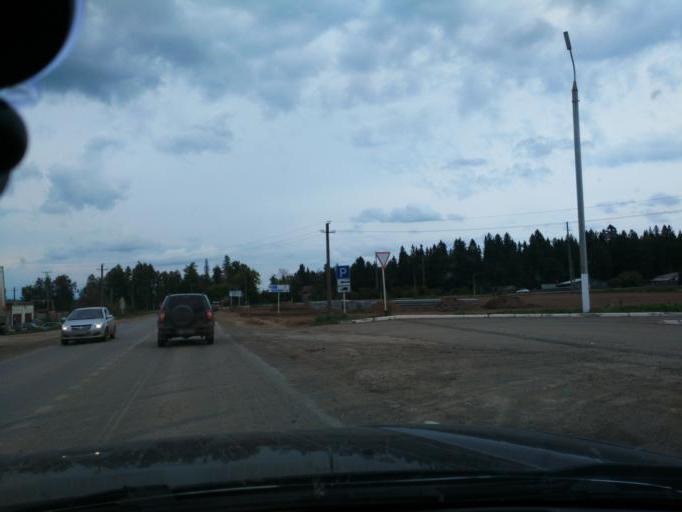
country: RU
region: Perm
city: Chernushka
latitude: 56.5326
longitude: 56.0924
